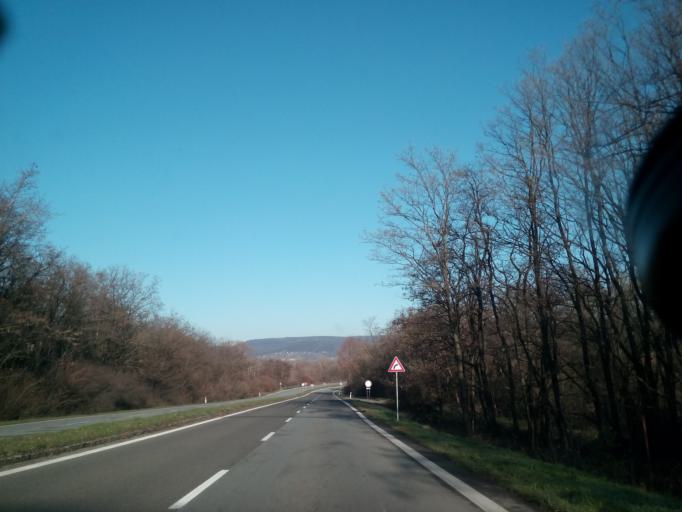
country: SK
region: Kosicky
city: Vinne
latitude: 48.7860
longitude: 21.9461
